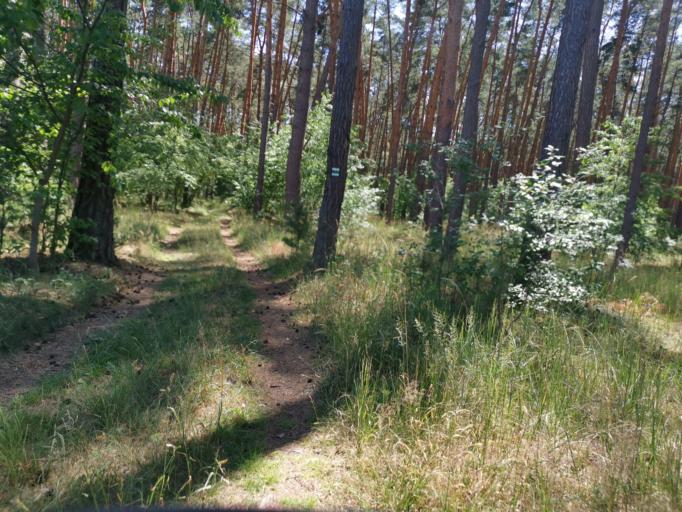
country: CZ
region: South Moravian
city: Rohatec
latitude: 48.9076
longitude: 17.2184
